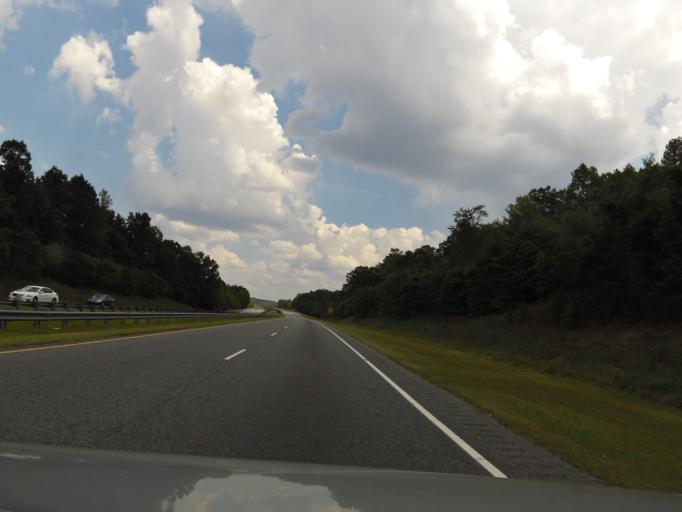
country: US
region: North Carolina
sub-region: Rutherford County
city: Rutherfordton
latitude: 35.2964
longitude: -81.9727
